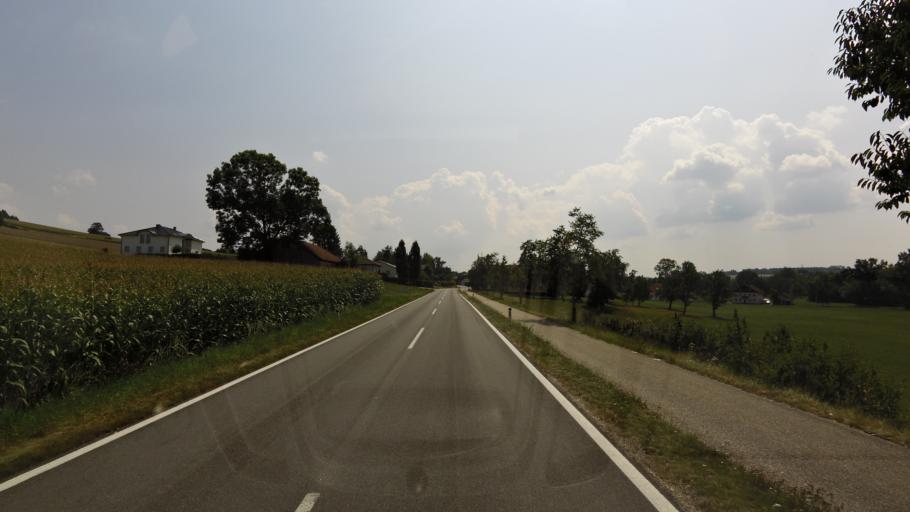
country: AT
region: Upper Austria
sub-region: Politischer Bezirk Ried im Innkreis
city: Waldzell
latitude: 48.1995
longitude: 13.3748
